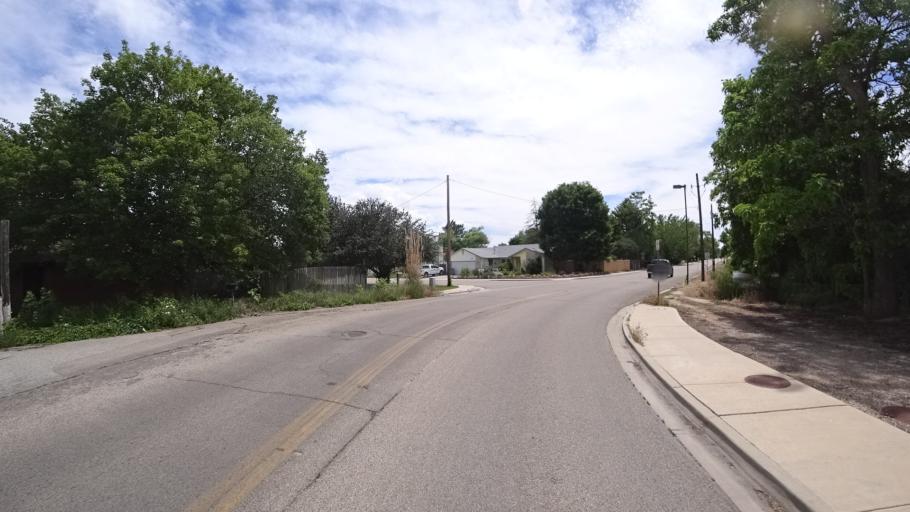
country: US
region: Idaho
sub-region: Ada County
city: Meridian
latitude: 43.6260
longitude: -116.3202
